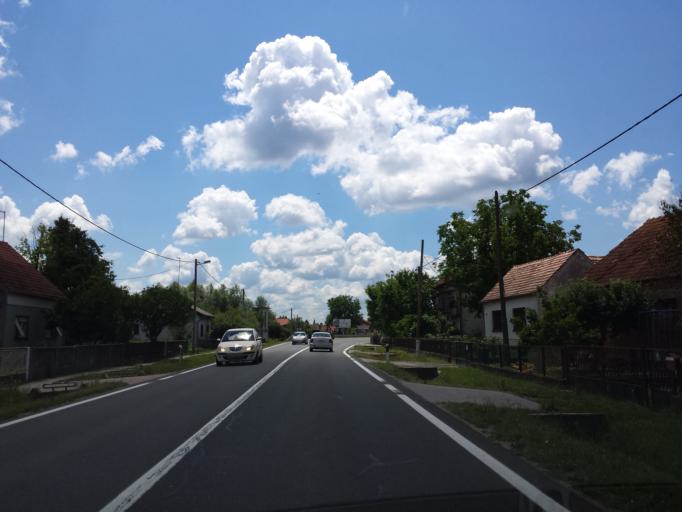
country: HR
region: Sisacko-Moslavacka
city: Lekenik
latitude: 45.5423
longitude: 16.2359
